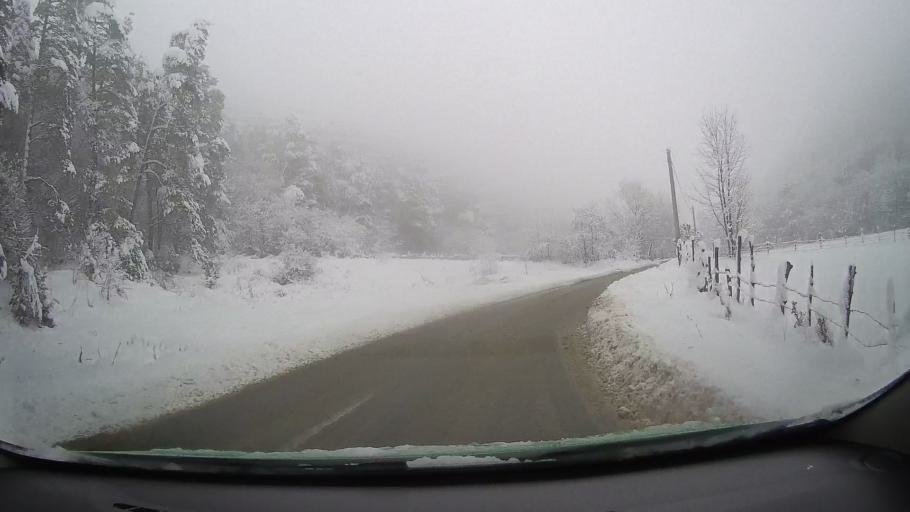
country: RO
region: Sibiu
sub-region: Comuna Tilisca
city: Tilisca
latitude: 45.8024
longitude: 23.8229
